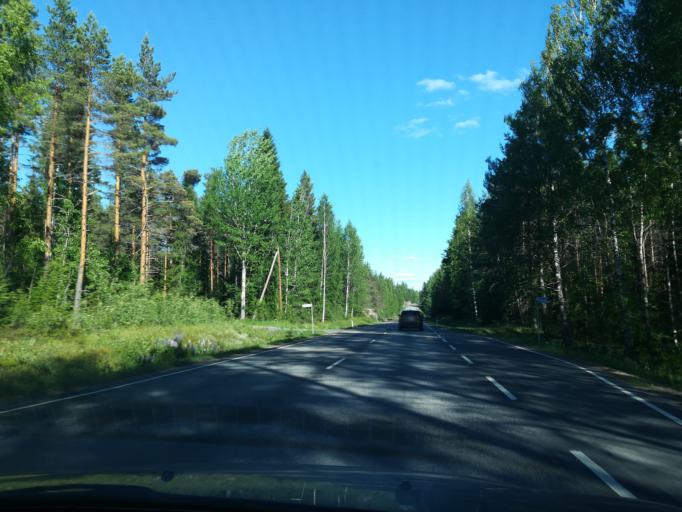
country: FI
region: South Karelia
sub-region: Imatra
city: Ruokolahti
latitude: 61.3653
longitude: 28.6883
